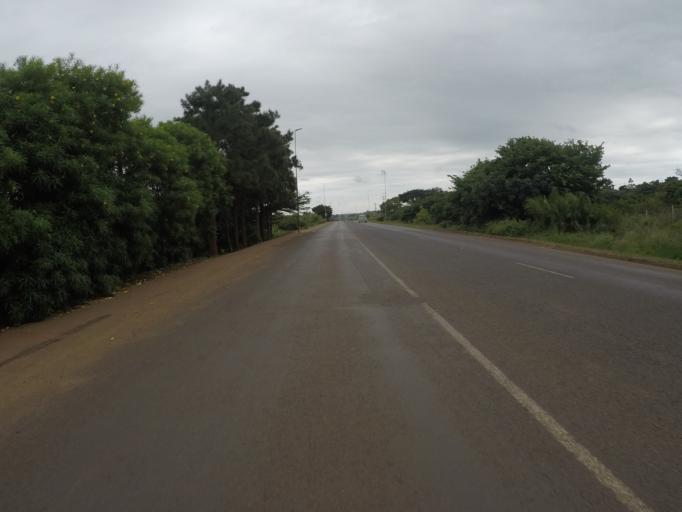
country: ZA
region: KwaZulu-Natal
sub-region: uThungulu District Municipality
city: Empangeni
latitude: -28.7739
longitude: 31.8690
